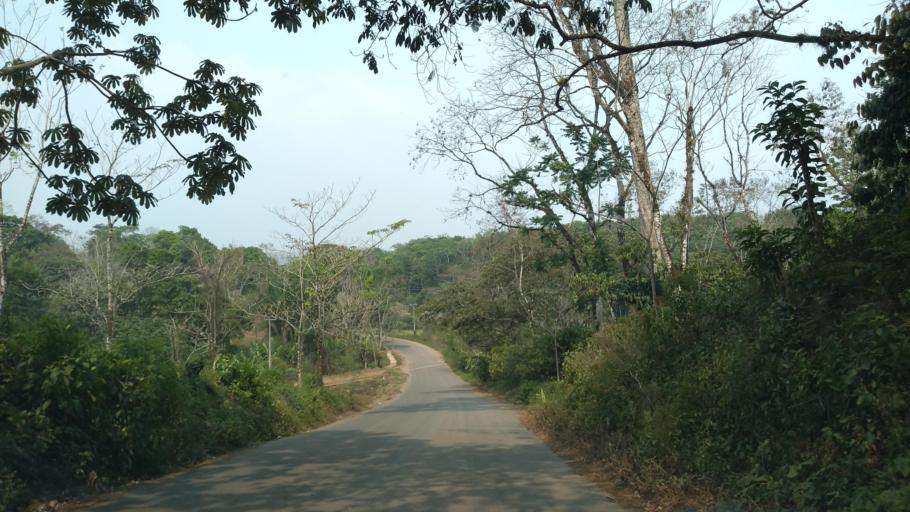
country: MX
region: Veracruz
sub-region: Tezonapa
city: Laguna Chica (Pueblo Nuevo)
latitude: 18.5420
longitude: -96.7738
